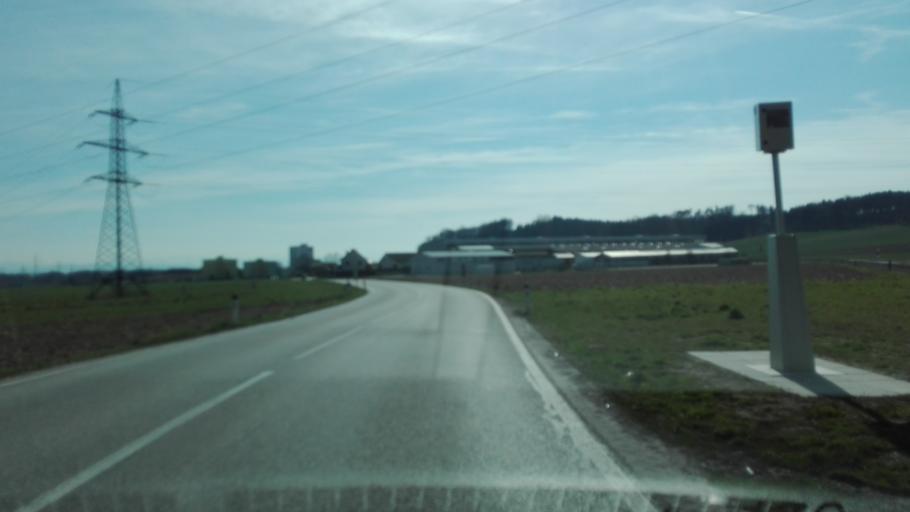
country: AT
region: Lower Austria
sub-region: Politischer Bezirk Amstetten
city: Ennsdorf
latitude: 48.2514
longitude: 14.5406
